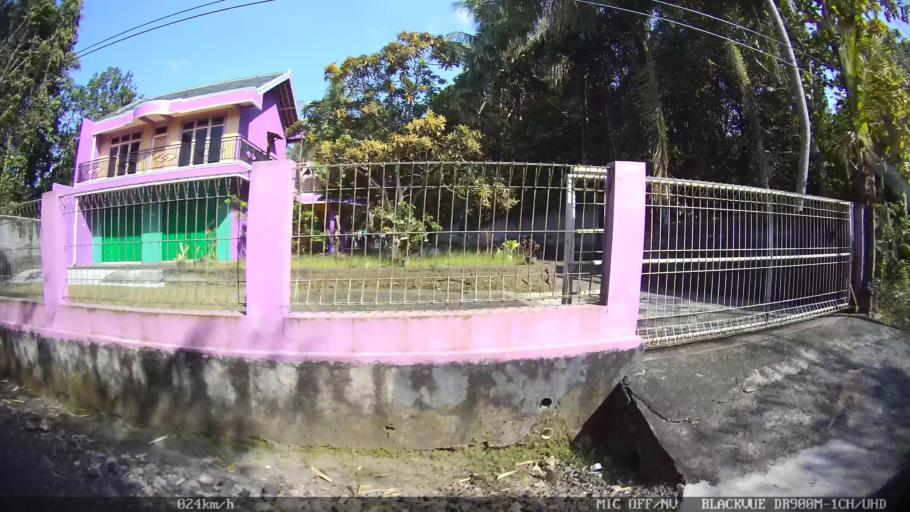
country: ID
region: Daerah Istimewa Yogyakarta
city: Kasihan
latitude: -7.8263
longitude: 110.2889
